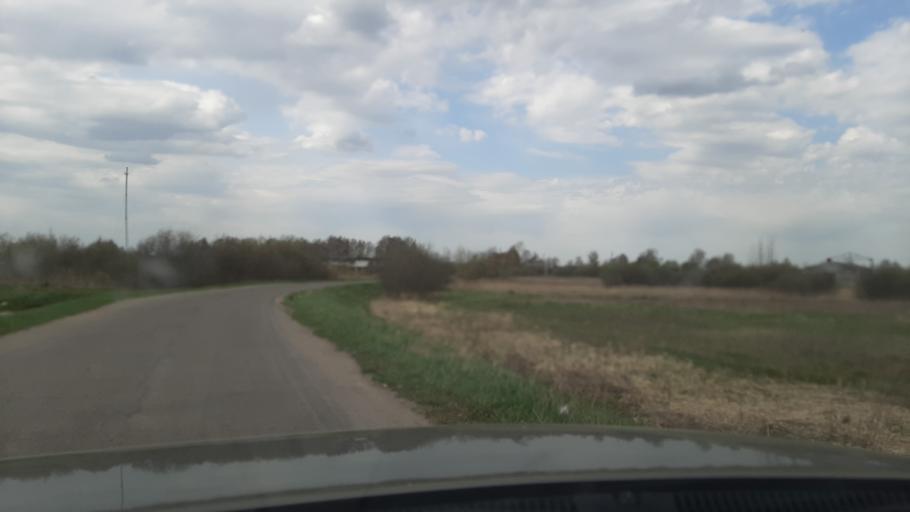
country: RU
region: Ivanovo
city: Privolzhsk
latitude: 57.3264
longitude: 41.2378
